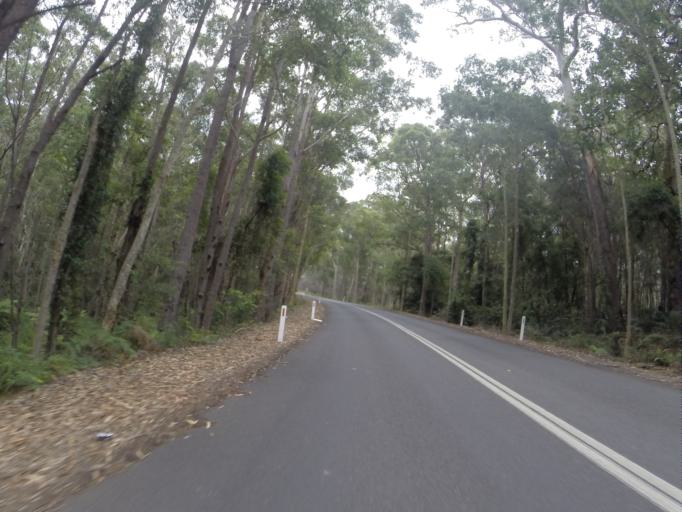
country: AU
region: New South Wales
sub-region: Eurobodalla
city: Batemans Bay
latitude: -35.6567
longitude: 150.2878
